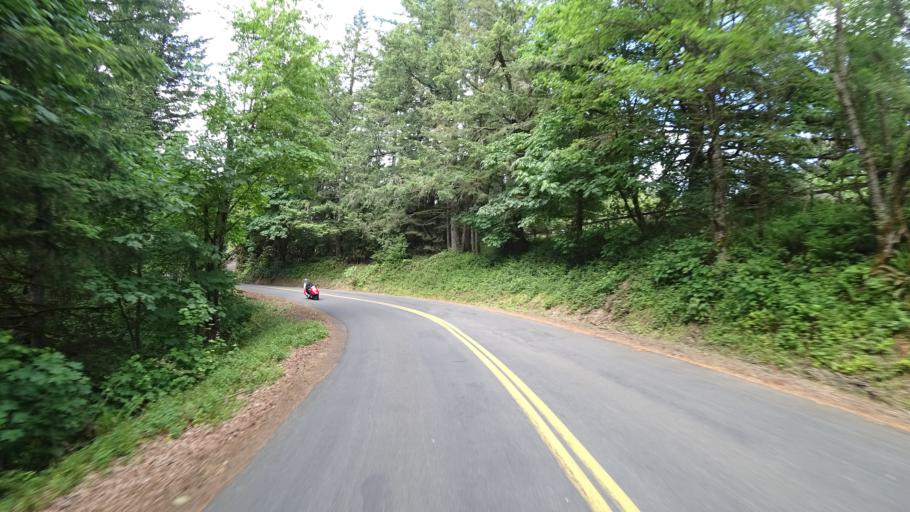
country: US
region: Oregon
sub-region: Washington County
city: Bethany
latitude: 45.6115
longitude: -122.8316
